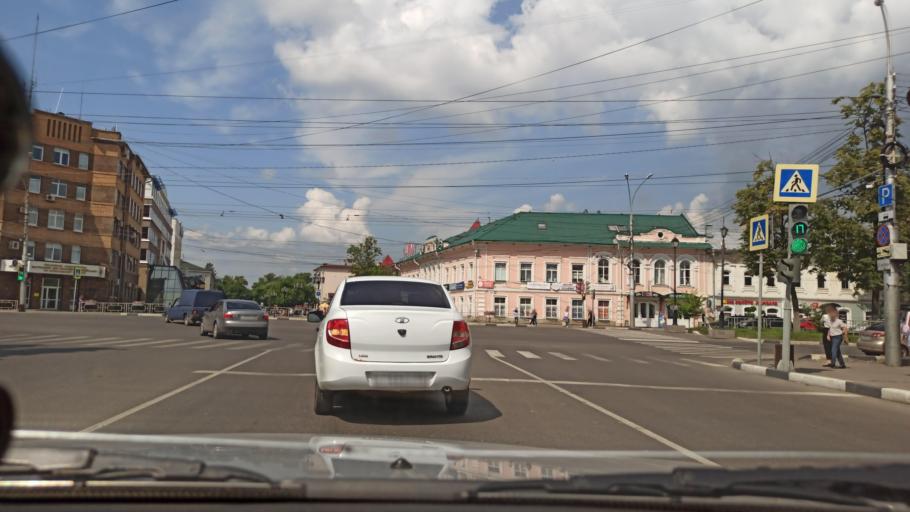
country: RU
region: Vologda
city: Vologda
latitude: 59.2194
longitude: 39.8870
